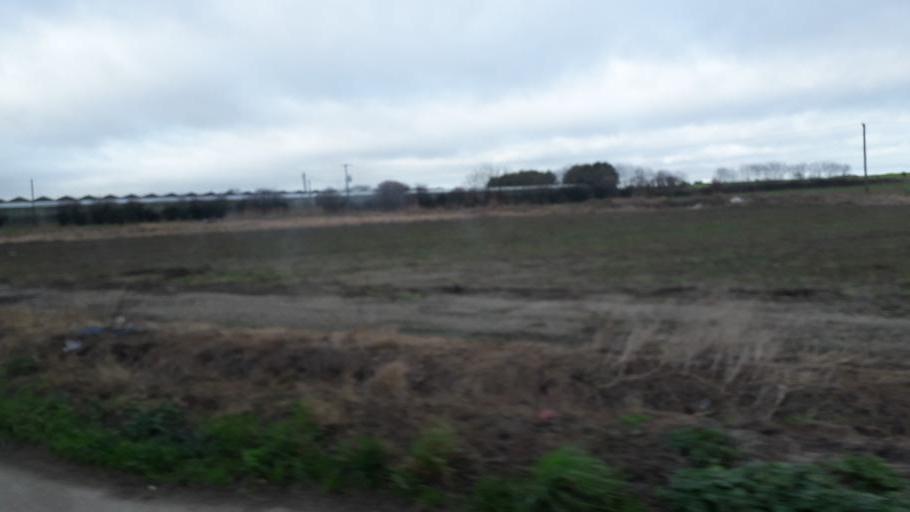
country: IE
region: Leinster
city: An Ros
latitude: 53.5180
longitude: -6.1181
